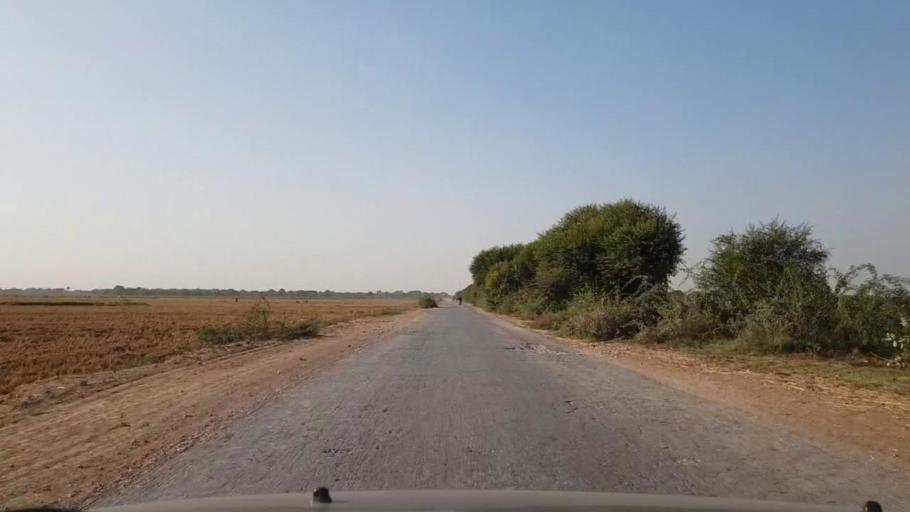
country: PK
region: Sindh
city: Chambar
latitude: 25.2009
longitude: 68.7946
